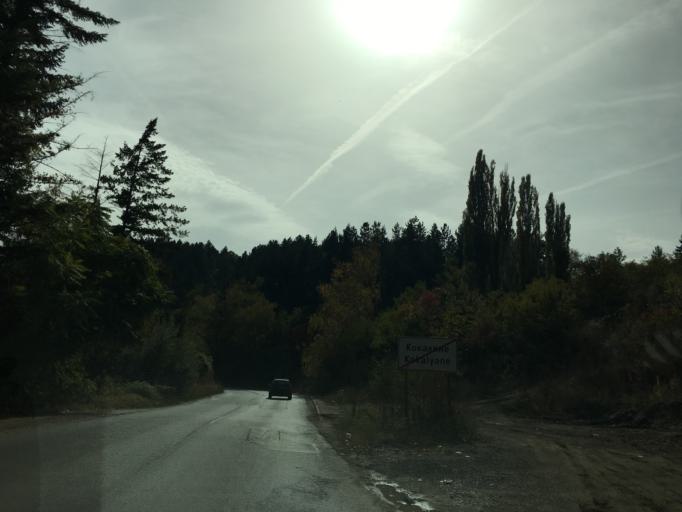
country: BG
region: Sofia-Capital
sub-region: Stolichna Obshtina
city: Sofia
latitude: 42.5793
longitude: 23.4251
